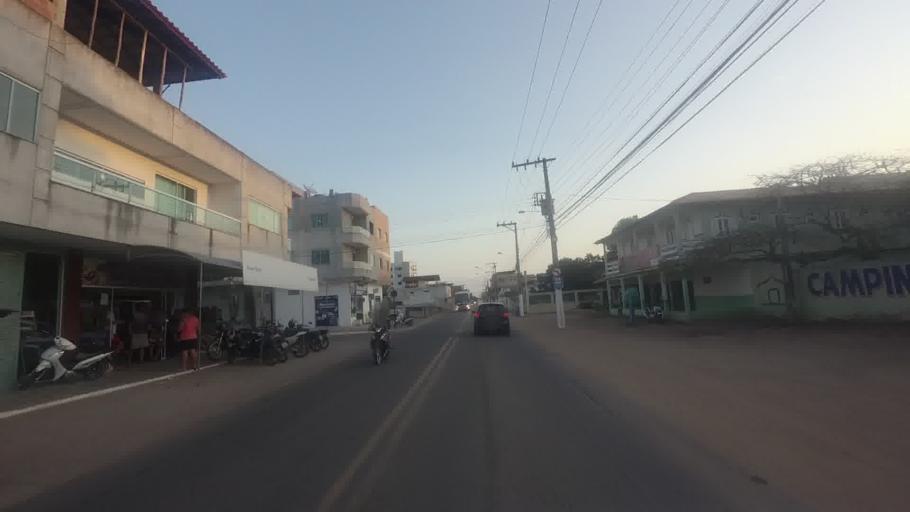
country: BR
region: Espirito Santo
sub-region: Piuma
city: Piuma
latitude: -20.8971
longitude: -40.7770
